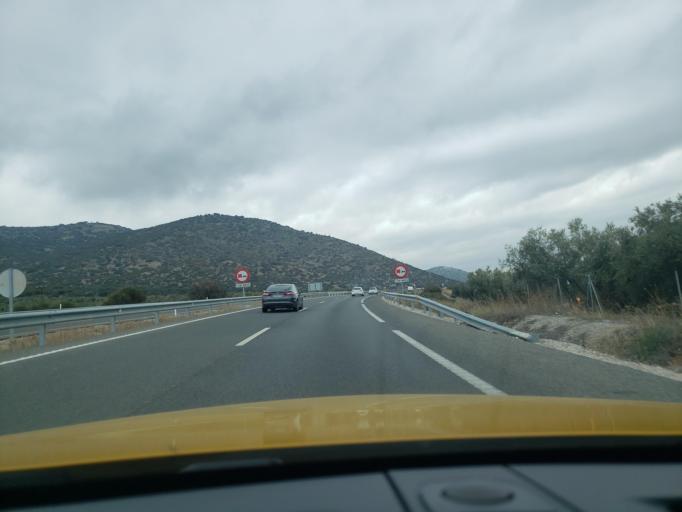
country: ES
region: Andalusia
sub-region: Provincia de Granada
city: Iznalloz
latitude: 37.3886
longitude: -3.5831
